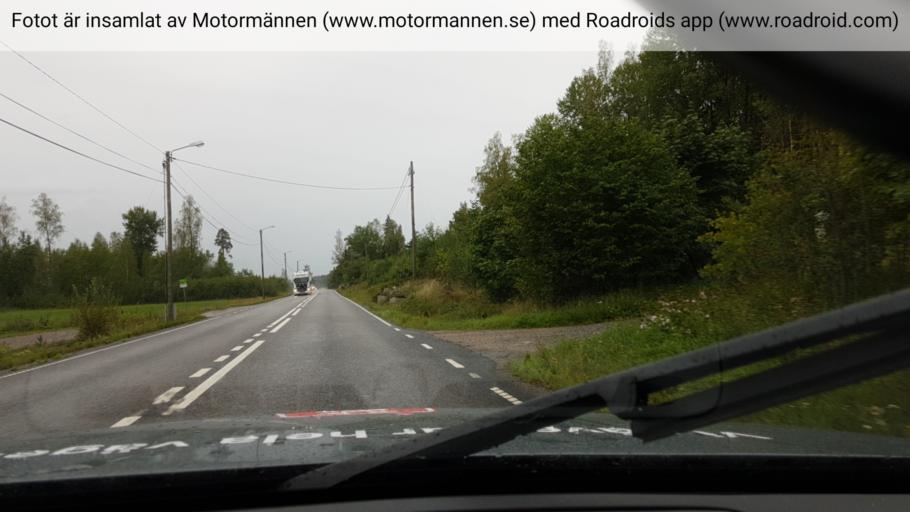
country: SE
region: Soedermanland
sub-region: Eskilstuna Kommun
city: Eskilstuna
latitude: 59.3334
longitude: 16.5291
